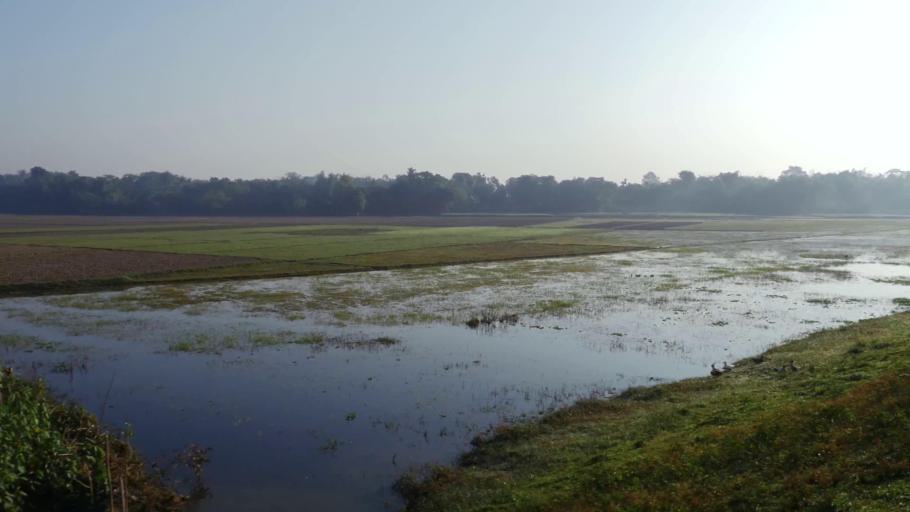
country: BD
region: Dhaka
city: Jamalpur
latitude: 24.9173
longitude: 89.9467
